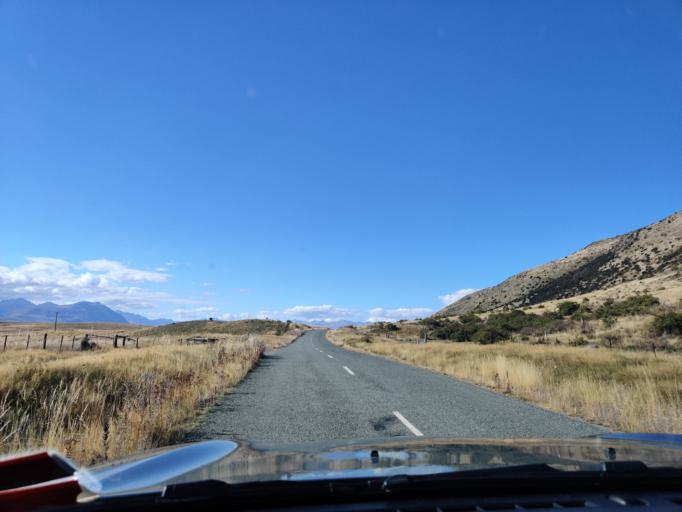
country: NZ
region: Canterbury
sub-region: Timaru District
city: Pleasant Point
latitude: -43.9837
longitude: 170.4573
